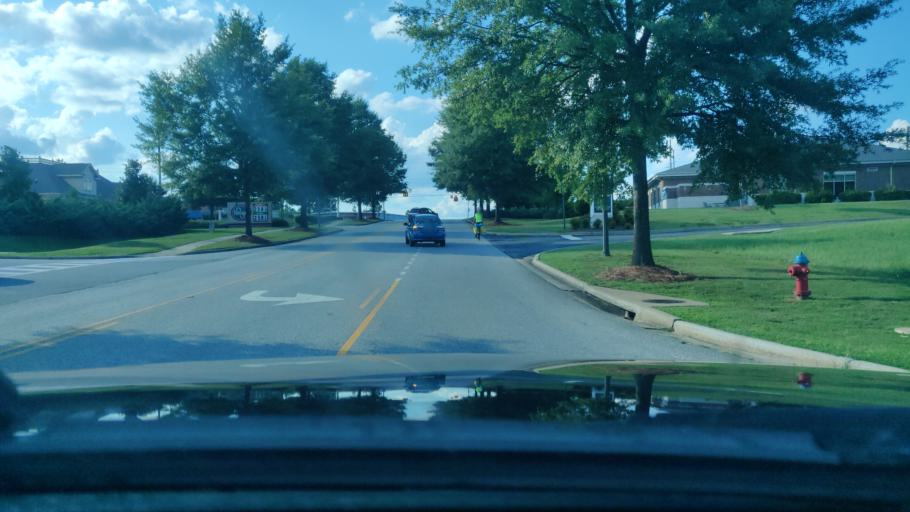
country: US
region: Alabama
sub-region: Lee County
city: Opelika
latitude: 32.6208
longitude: -85.4092
